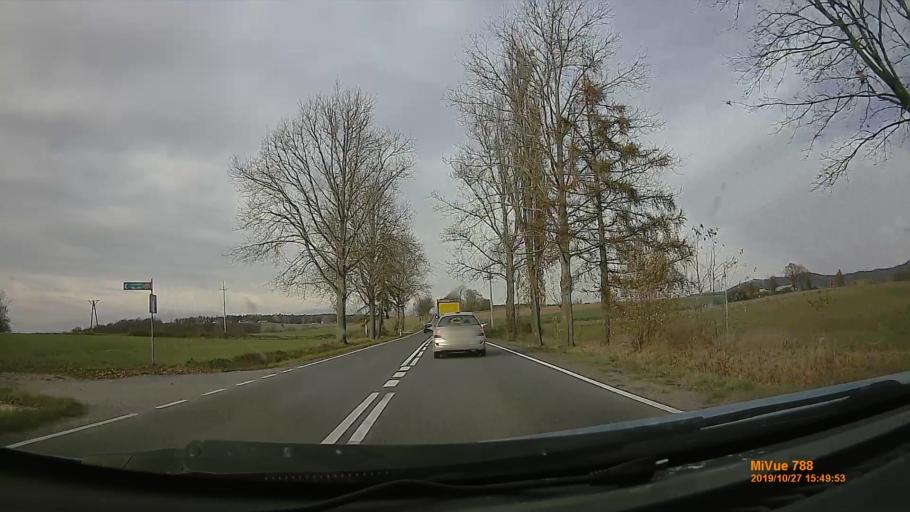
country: PL
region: Lower Silesian Voivodeship
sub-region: Powiat klodzki
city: Bozkow
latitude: 50.5122
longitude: 16.5847
